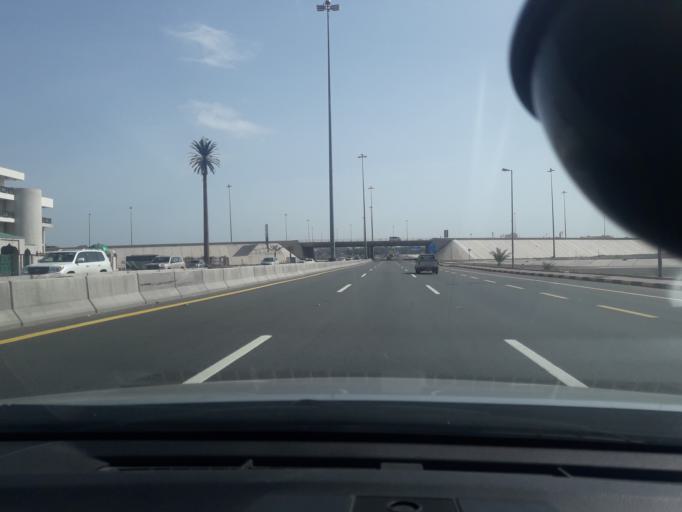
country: SA
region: Al Madinah al Munawwarah
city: Medina
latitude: 24.4410
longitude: 39.6234
